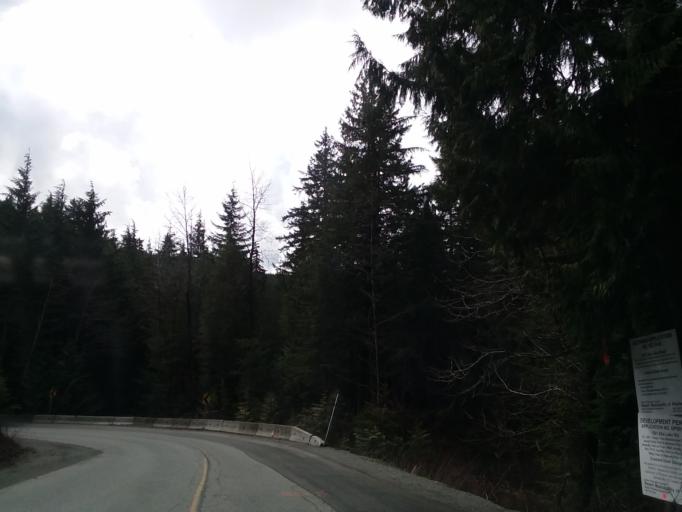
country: CA
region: British Columbia
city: Whistler
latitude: 50.0918
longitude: -123.0128
